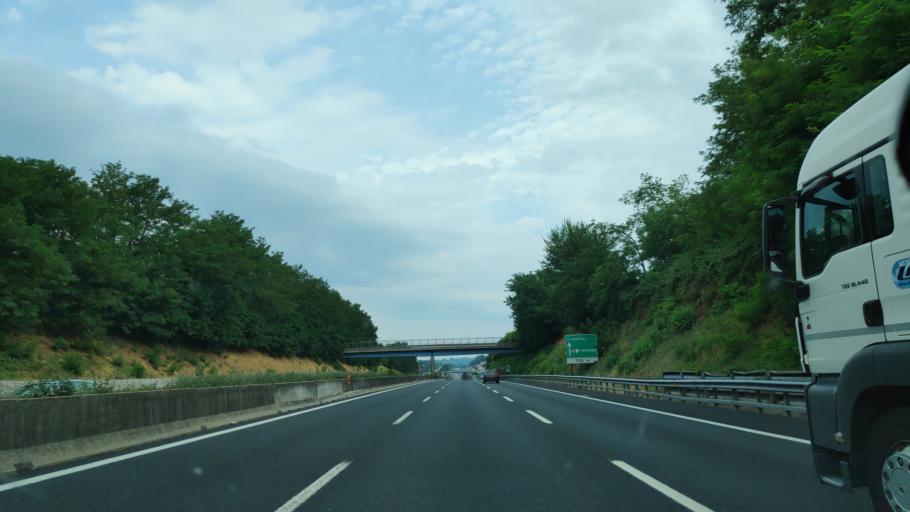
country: IT
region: Latium
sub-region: Provincia di Frosinone
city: Frosinone
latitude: 41.6242
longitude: 13.2992
